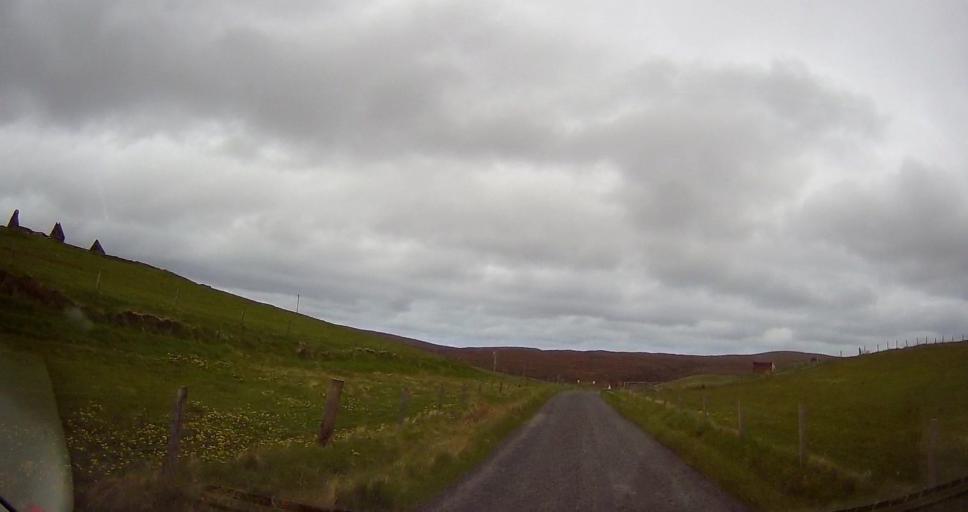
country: GB
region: Scotland
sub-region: Shetland Islands
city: Shetland
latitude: 60.7996
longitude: -0.8725
